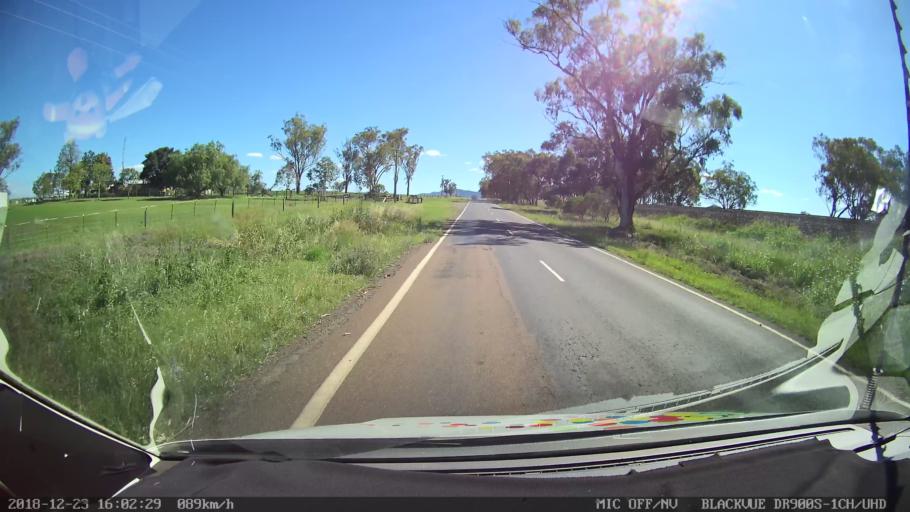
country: AU
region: New South Wales
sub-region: Tamworth Municipality
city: Phillip
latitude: -31.2327
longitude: 150.8087
